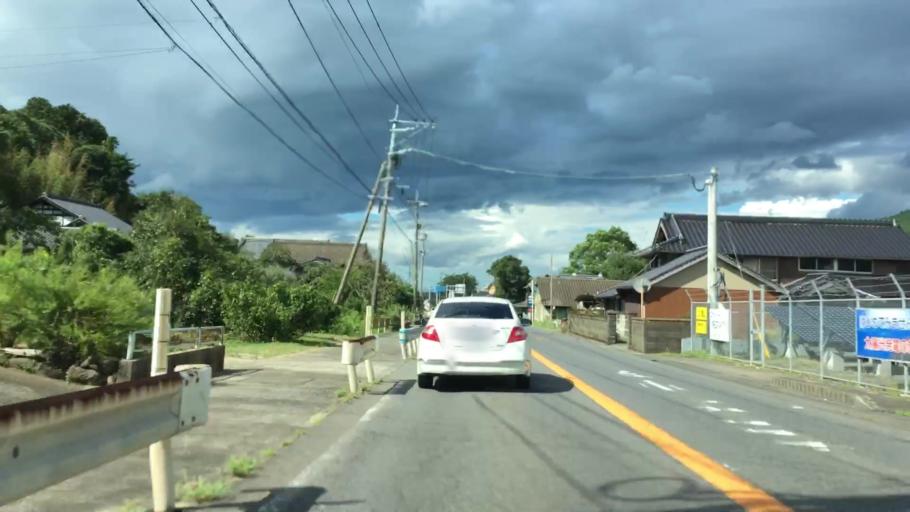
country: JP
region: Saga Prefecture
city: Imaricho-ko
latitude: 33.2305
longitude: 129.8490
